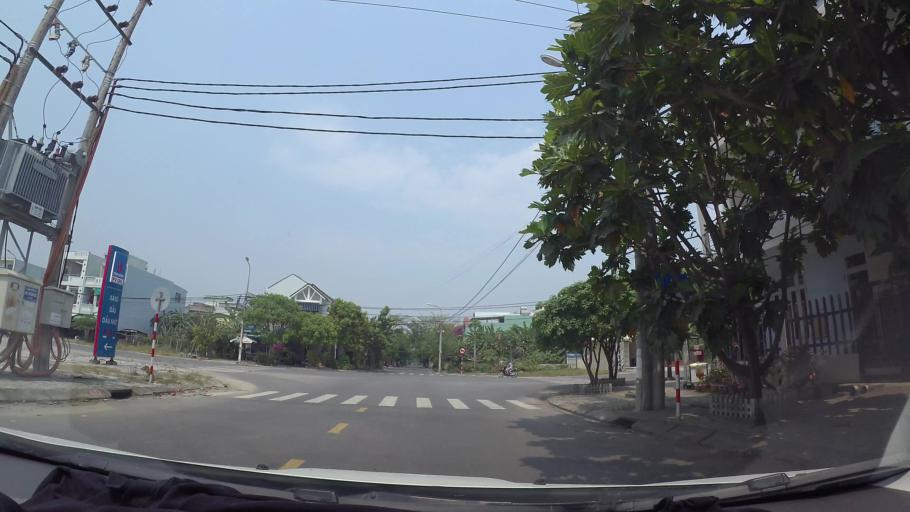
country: VN
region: Da Nang
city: Cam Le
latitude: 16.0033
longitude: 108.2177
